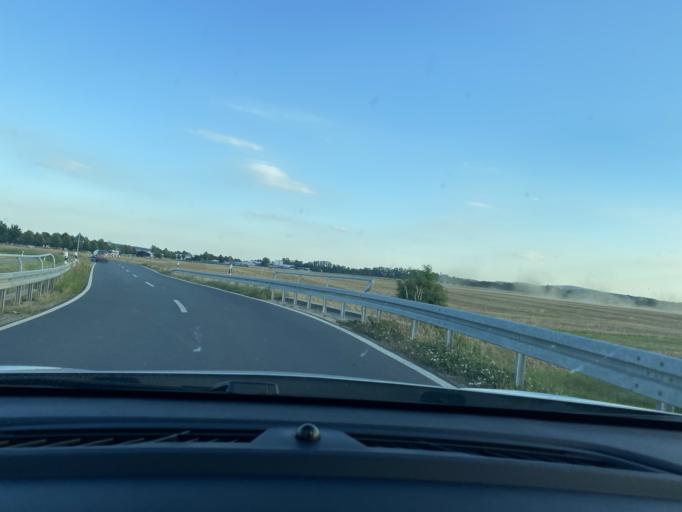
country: DE
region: Saxony
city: Kodersdorf
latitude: 51.2545
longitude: 14.8876
